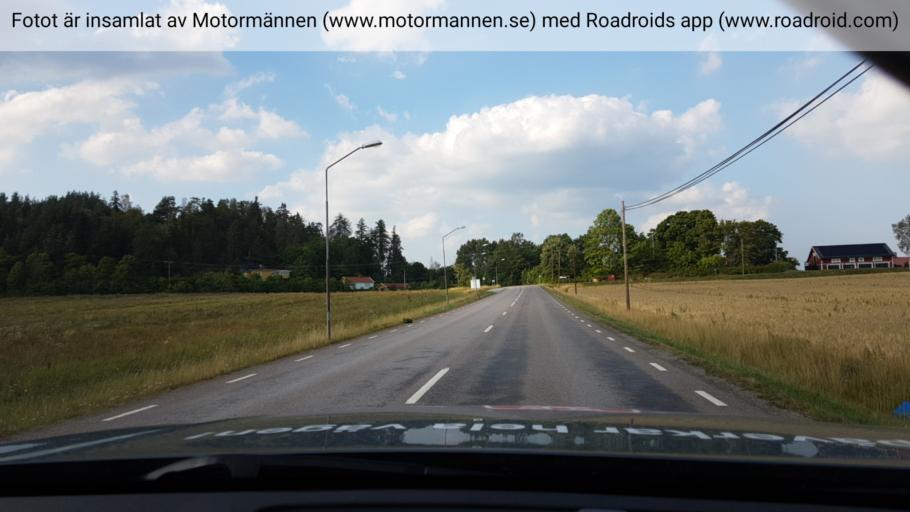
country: SE
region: Soedermanland
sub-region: Gnesta Kommun
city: Gnesta
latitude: 59.0567
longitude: 17.3044
